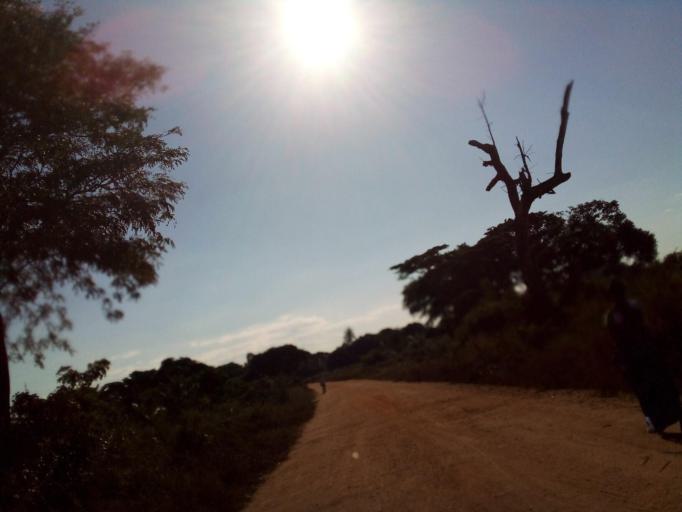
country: MZ
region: Zambezia
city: Quelimane
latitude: -17.5134
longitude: 36.6031
